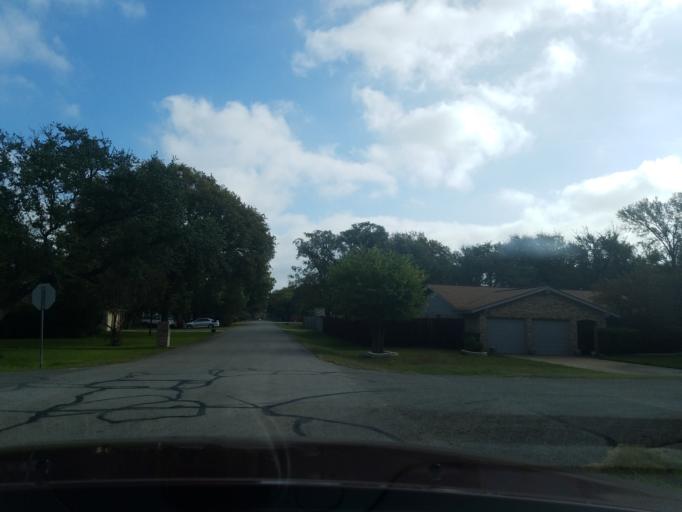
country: US
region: Texas
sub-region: Williamson County
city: Jollyville
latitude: 30.4536
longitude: -97.7843
